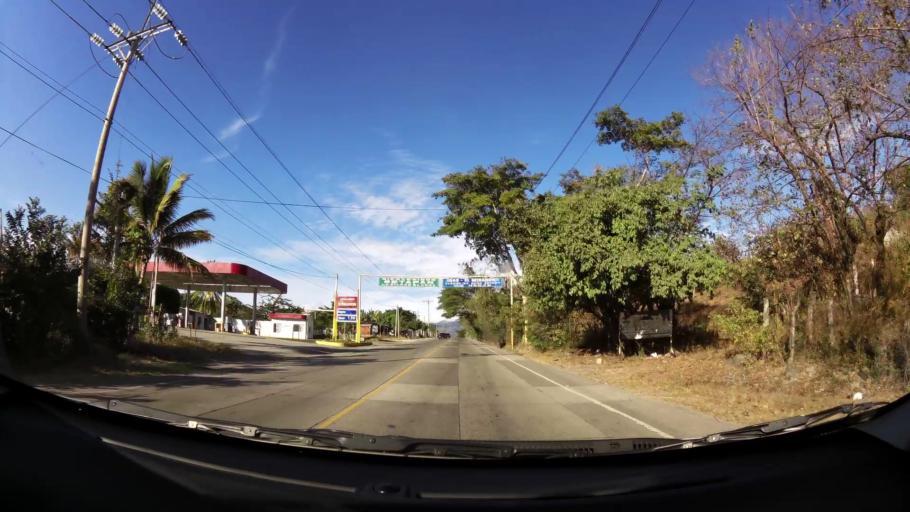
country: SV
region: Santa Ana
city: Metapan
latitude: 14.3071
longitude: -89.4535
